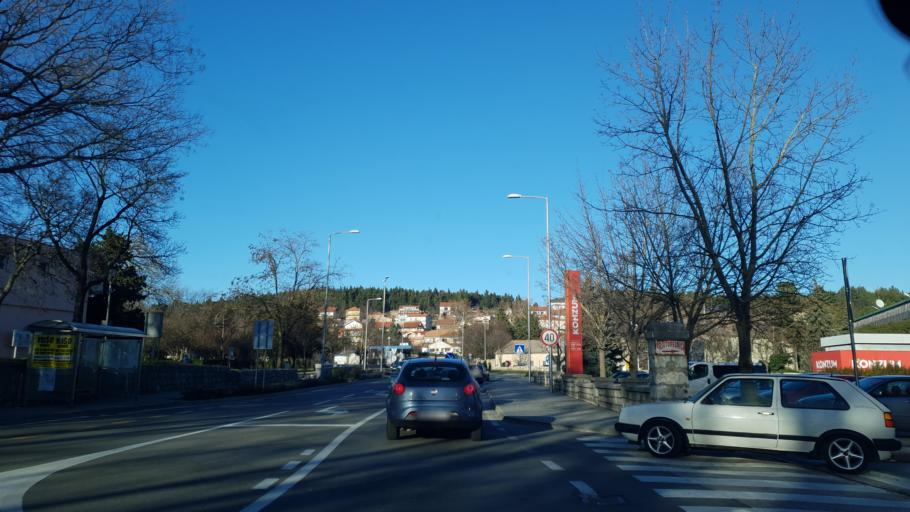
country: HR
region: Splitsko-Dalmatinska
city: Sinj
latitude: 43.7024
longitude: 16.6422
